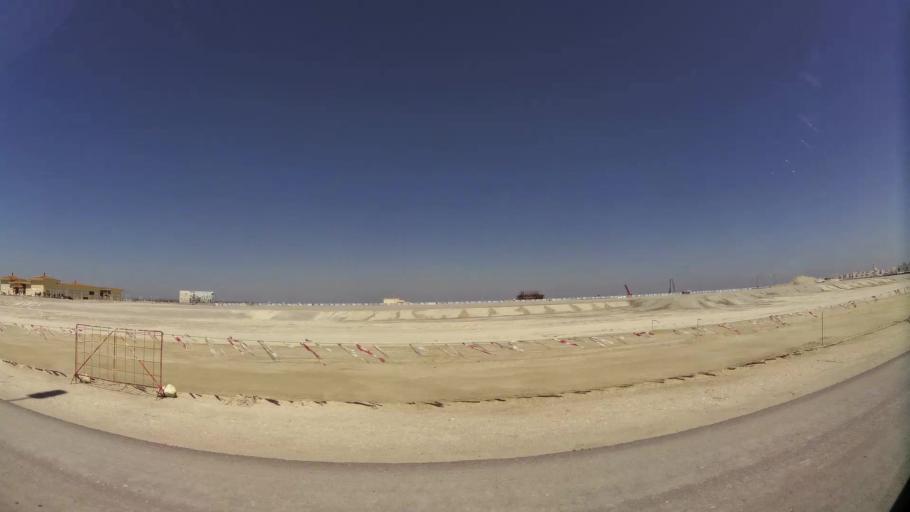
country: BH
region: Muharraq
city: Al Muharraq
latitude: 26.3026
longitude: 50.6282
